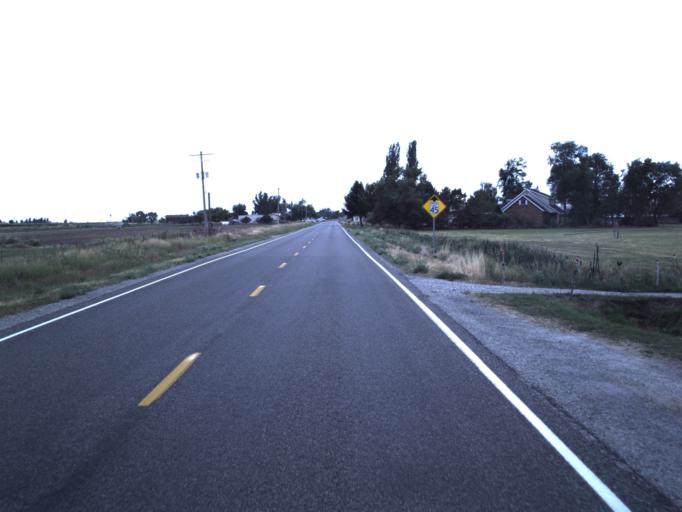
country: US
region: Utah
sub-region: Cache County
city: Lewiston
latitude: 41.9811
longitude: -111.9544
